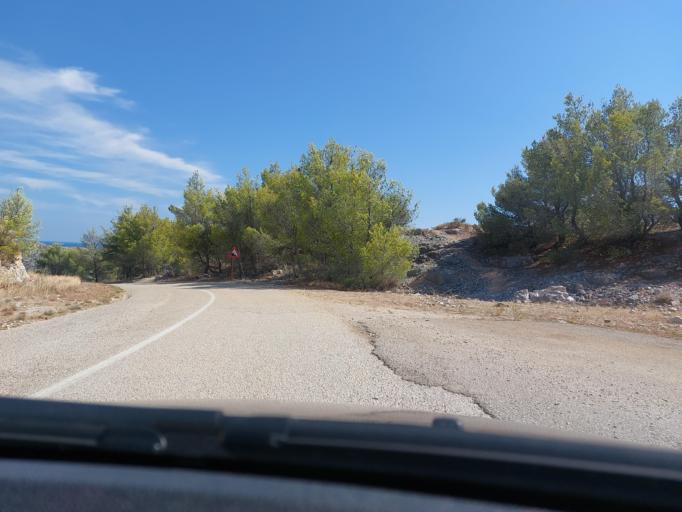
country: HR
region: Dubrovacko-Neretvanska
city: Smokvica
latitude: 42.7445
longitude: 16.8732
